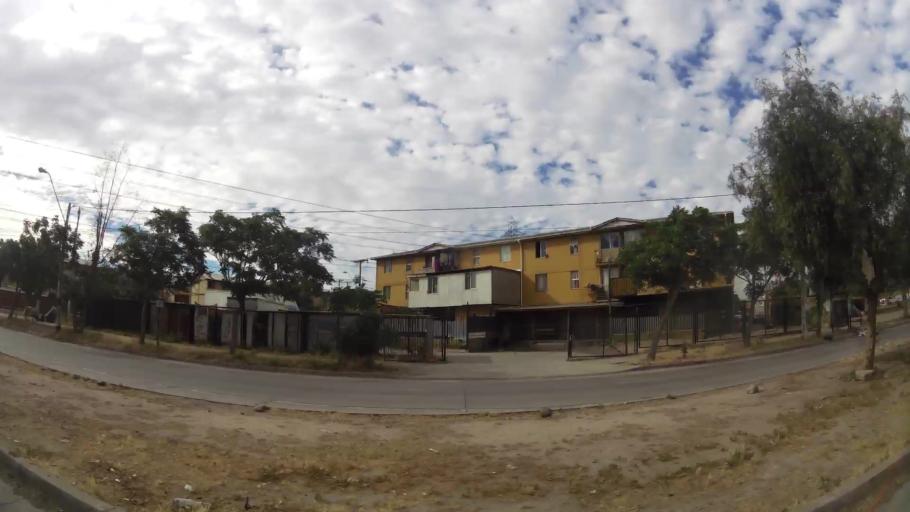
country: CL
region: Santiago Metropolitan
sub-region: Provincia de Santiago
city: La Pintana
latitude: -33.6232
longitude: -70.6201
